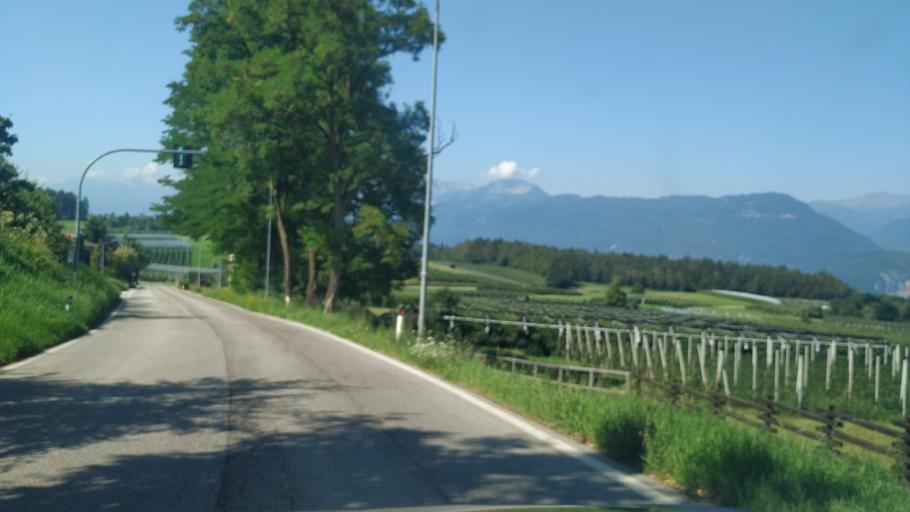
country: IT
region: Trentino-Alto Adige
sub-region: Provincia di Trento
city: Romeno
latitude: 46.3921
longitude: 11.1171
